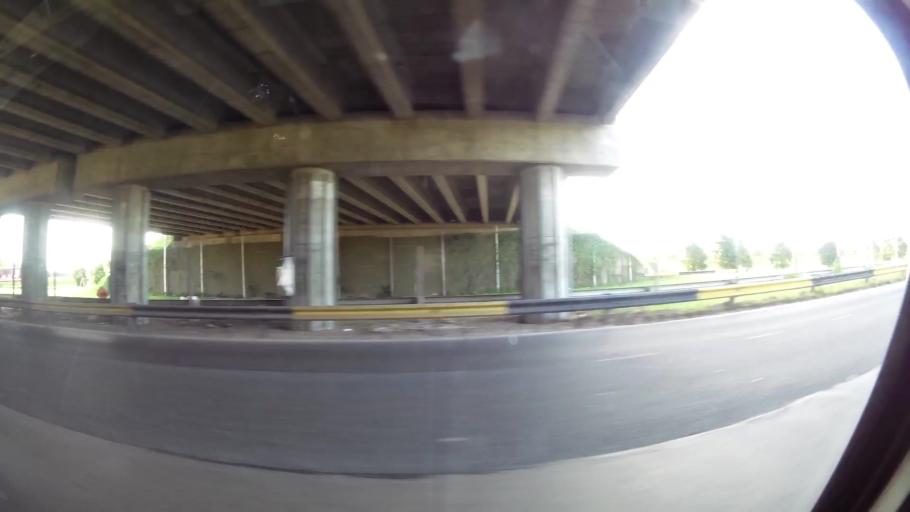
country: AR
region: Buenos Aires
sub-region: Partido de La Plata
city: La Plata
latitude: -34.8813
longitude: -57.9570
